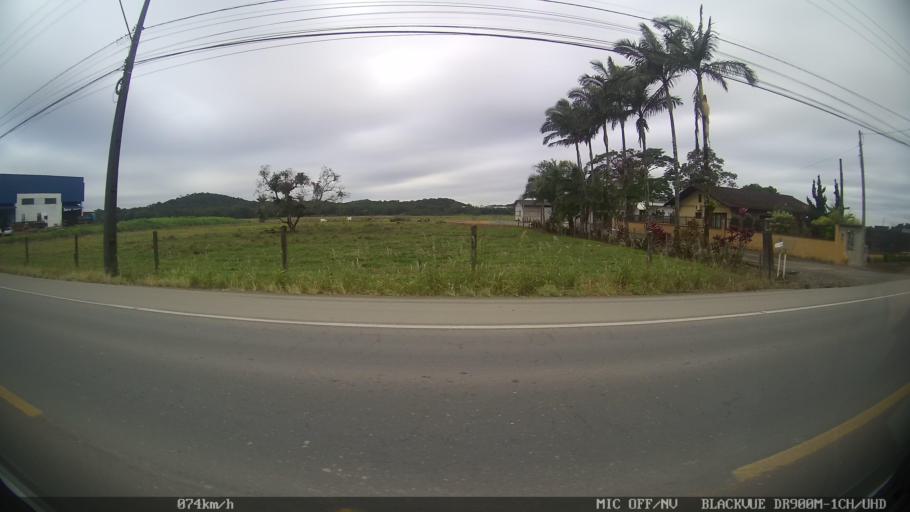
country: BR
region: Santa Catarina
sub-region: Joinville
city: Joinville
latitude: -26.2742
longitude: -48.9238
